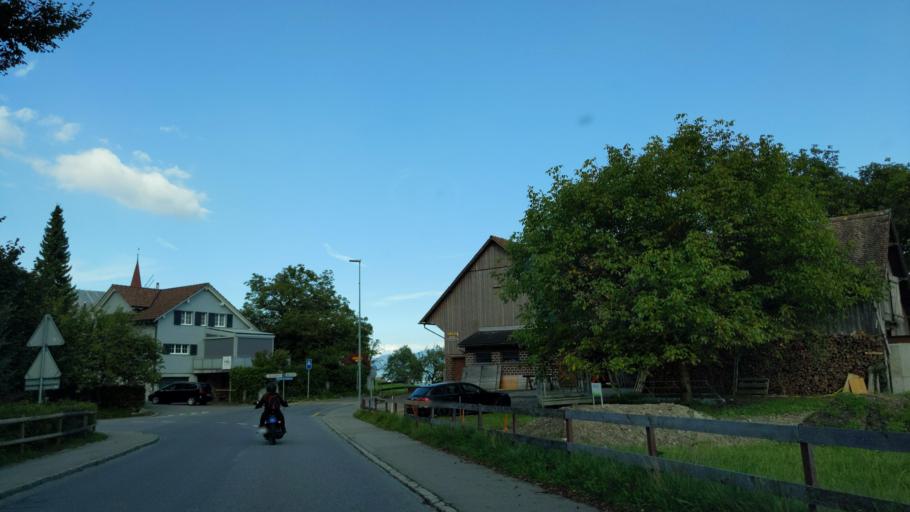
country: CH
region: Saint Gallen
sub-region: Wahlkreis Rheintal
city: Eichberg
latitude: 47.3453
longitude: 9.5234
